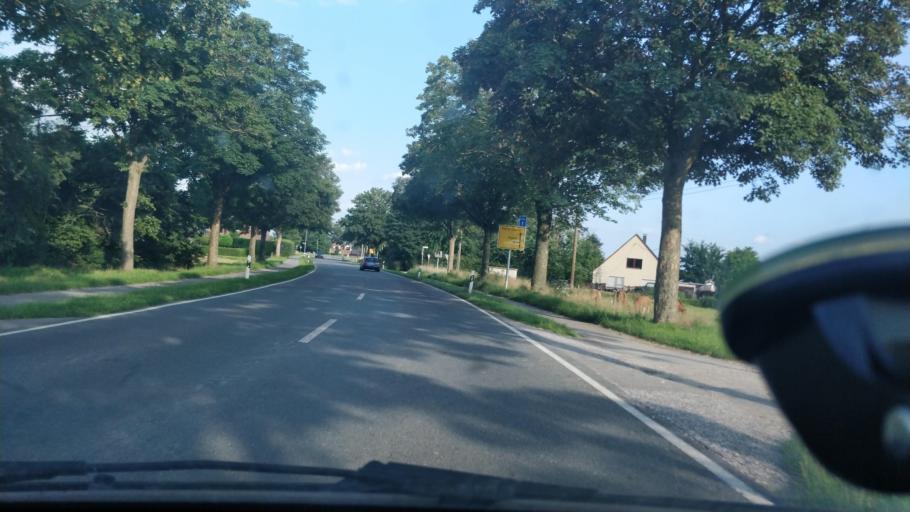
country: DE
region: North Rhine-Westphalia
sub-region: Regierungsbezirk Dusseldorf
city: Kamp-Lintfort
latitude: 51.5266
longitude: 6.5234
